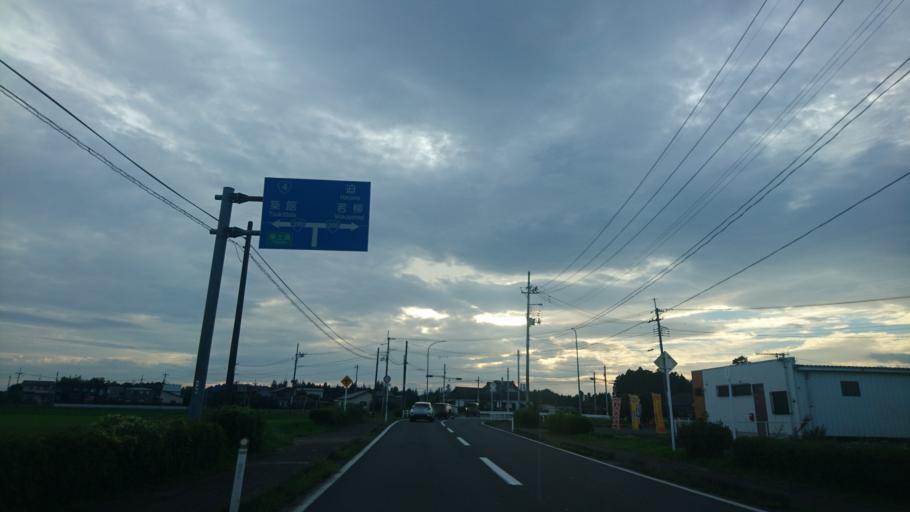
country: JP
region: Iwate
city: Ichinoseki
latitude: 38.7478
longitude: 141.0530
